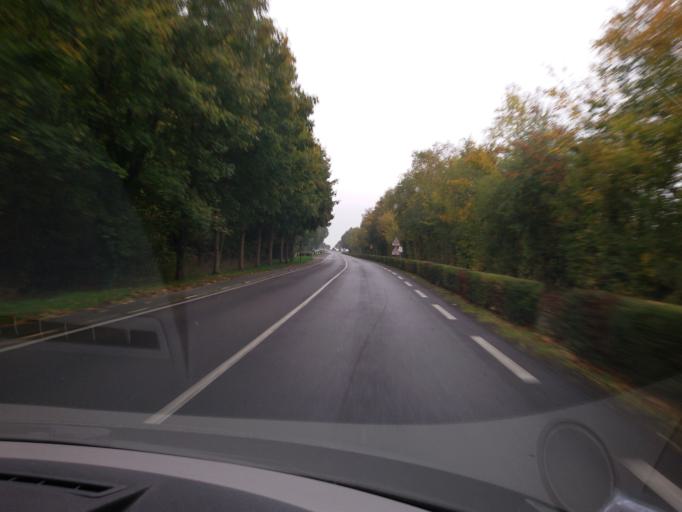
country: FR
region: Lower Normandy
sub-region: Departement du Calvados
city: Honfleur
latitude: 49.4253
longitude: 0.2221
